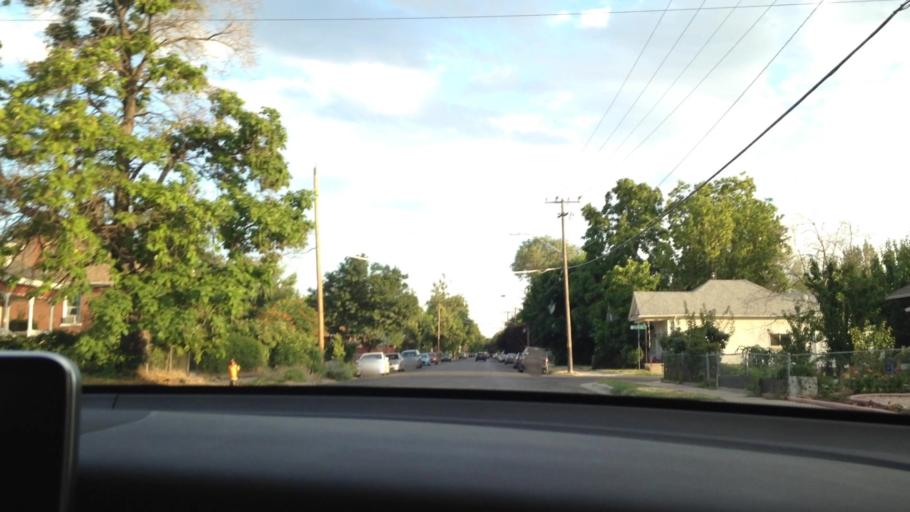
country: US
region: Utah
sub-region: Salt Lake County
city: South Salt Lake
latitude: 40.7327
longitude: -111.8797
